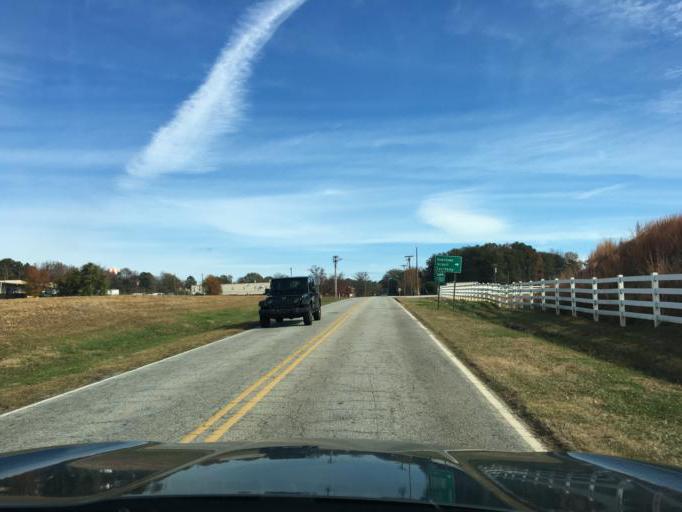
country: US
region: South Carolina
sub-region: Greenville County
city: Greenville
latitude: 34.8561
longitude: -82.3485
